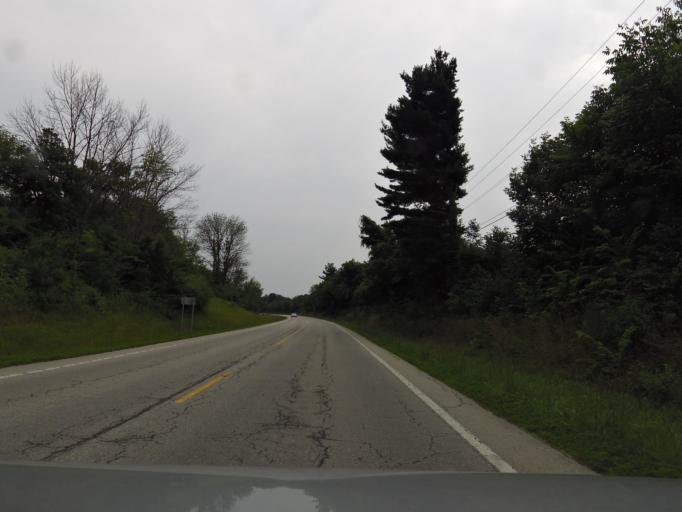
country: US
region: Ohio
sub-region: Clinton County
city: Wilmington
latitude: 39.3968
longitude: -83.8577
